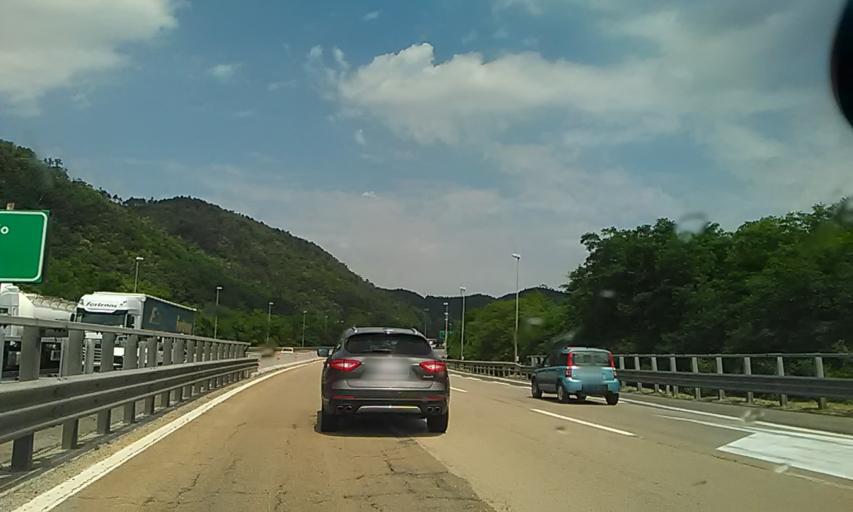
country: IT
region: Liguria
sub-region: Provincia di Genova
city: Rossiglione
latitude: 44.5881
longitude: 8.6647
